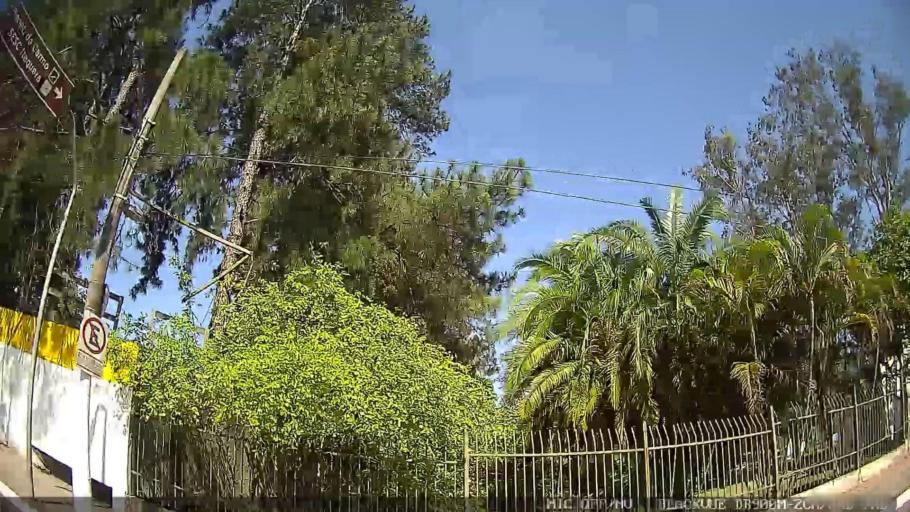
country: BR
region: Sao Paulo
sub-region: Sao Caetano Do Sul
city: Sao Caetano do Sul
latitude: -23.5675
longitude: -46.4683
